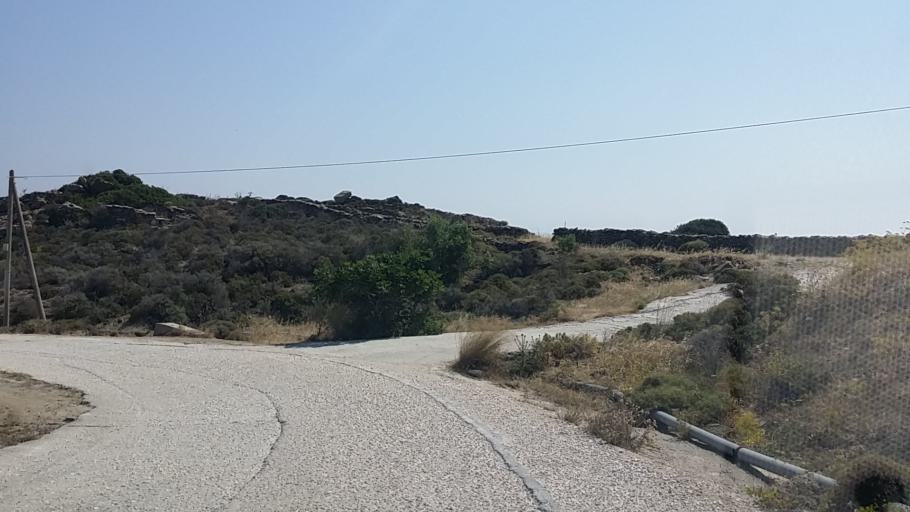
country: GR
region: South Aegean
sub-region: Nomos Kykladon
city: Paros
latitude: 37.0514
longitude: 25.2001
